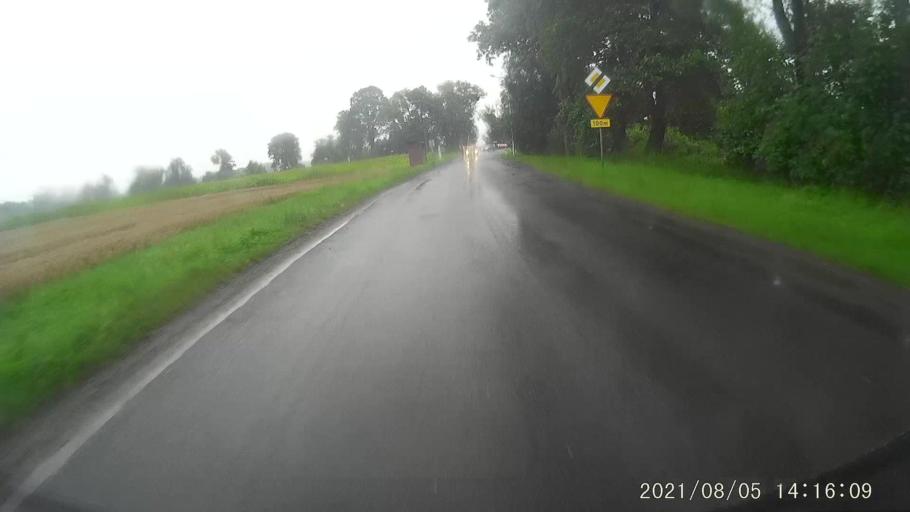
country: PL
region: Opole Voivodeship
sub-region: Powiat prudnicki
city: Biala
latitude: 50.4592
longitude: 17.7266
